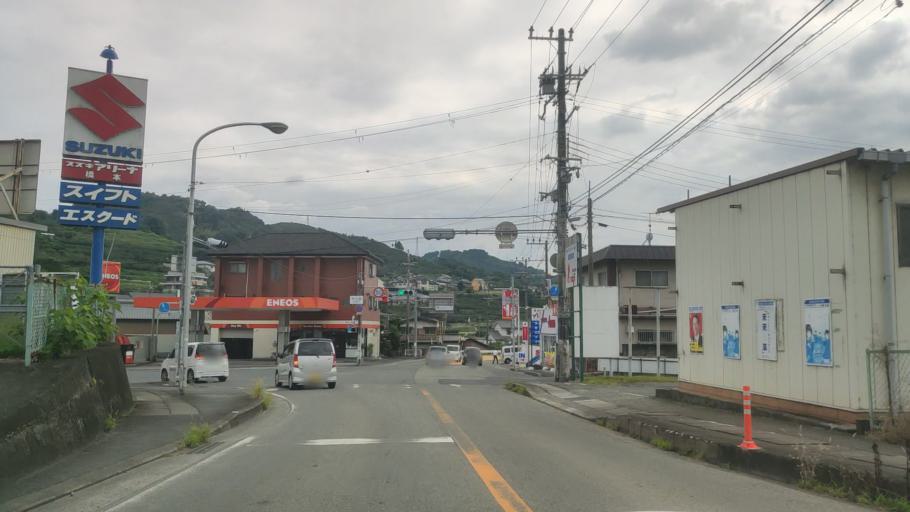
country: JP
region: Wakayama
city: Hashimoto
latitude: 34.2977
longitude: 135.5780
